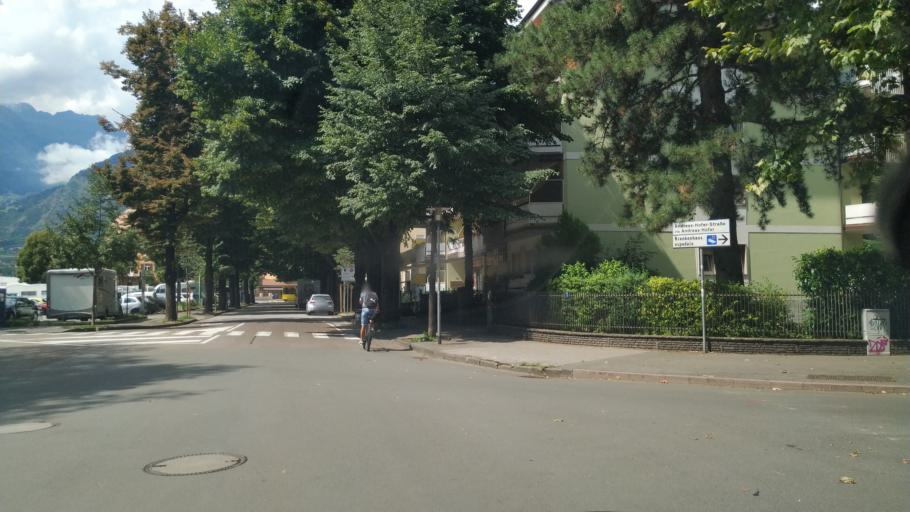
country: IT
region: Trentino-Alto Adige
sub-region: Bolzano
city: Merano
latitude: 46.6740
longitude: 11.1508
